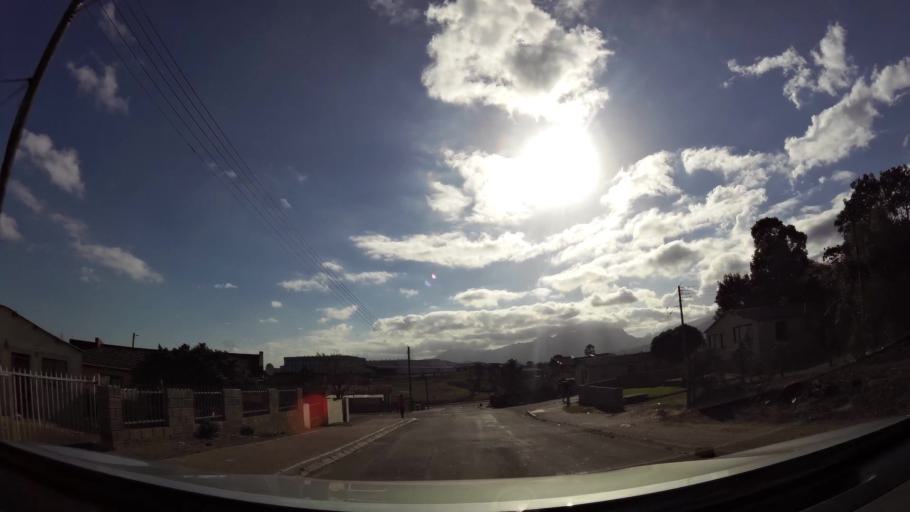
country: ZA
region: Western Cape
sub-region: Eden District Municipality
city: George
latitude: -33.9787
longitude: 22.4781
